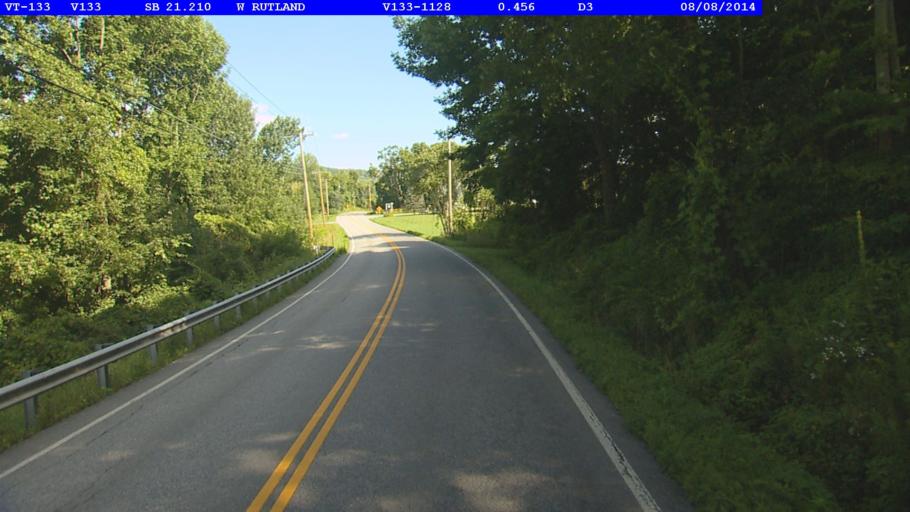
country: US
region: Vermont
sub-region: Rutland County
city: West Rutland
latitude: 43.5766
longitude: -73.0368
